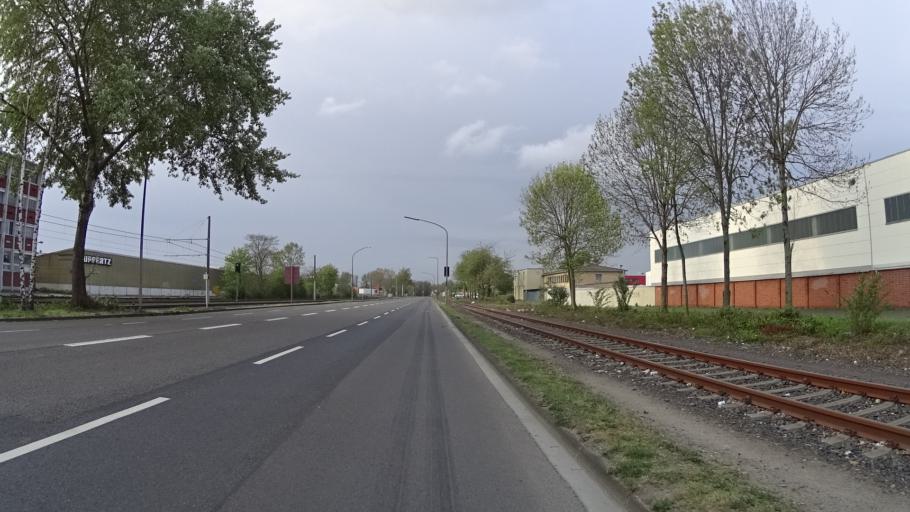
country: DE
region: North Rhine-Westphalia
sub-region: Regierungsbezirk Koln
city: Nippes
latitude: 51.0016
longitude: 6.9549
